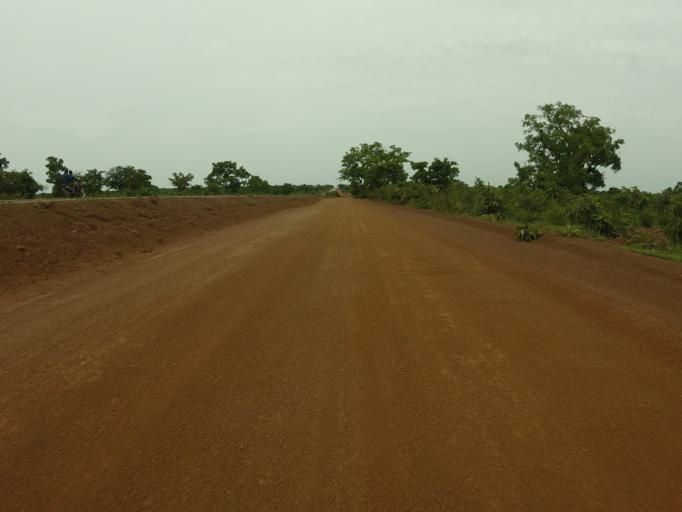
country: GH
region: Northern
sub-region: Yendi
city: Yendi
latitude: 9.0254
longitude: -0.0138
